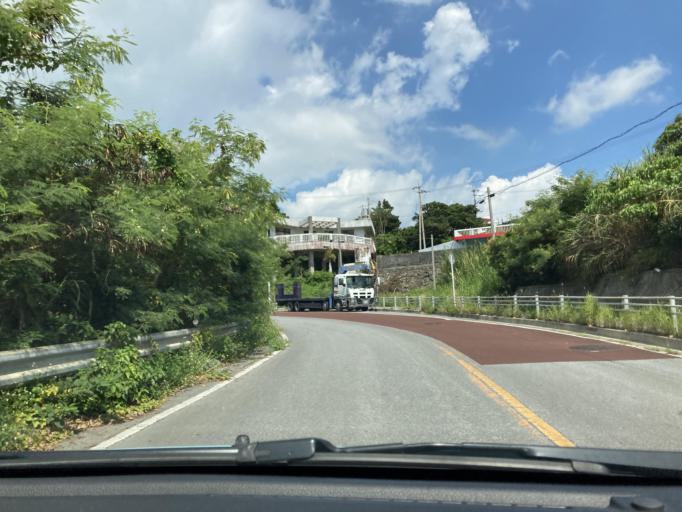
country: JP
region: Okinawa
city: Tomigusuku
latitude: 26.1414
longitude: 127.7709
